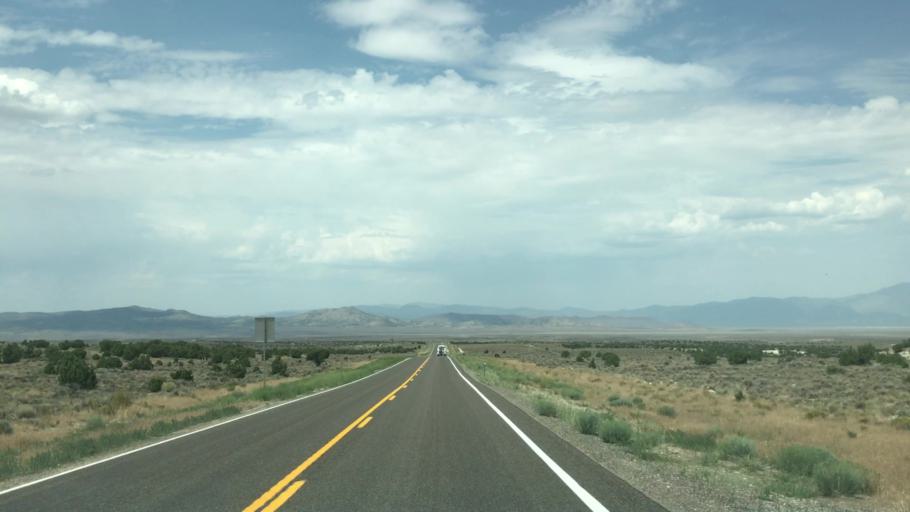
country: US
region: Nevada
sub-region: Eureka County
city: Eureka
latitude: 39.3920
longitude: -115.5095
